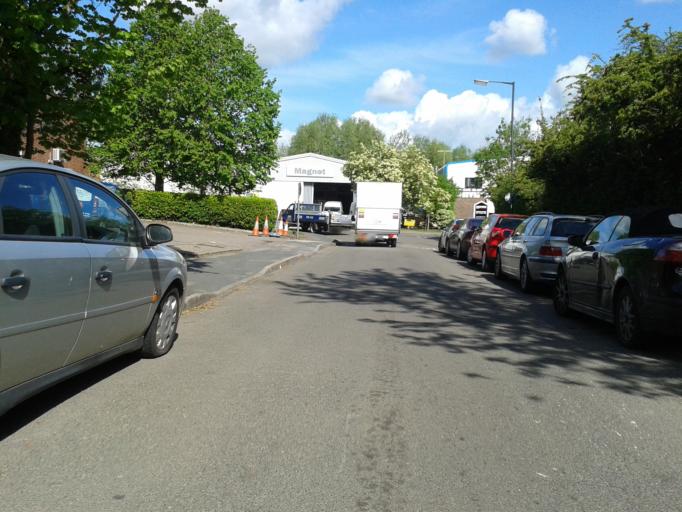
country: GB
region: England
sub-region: Cambridgeshire
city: Cambridge
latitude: 52.2145
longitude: 0.1504
